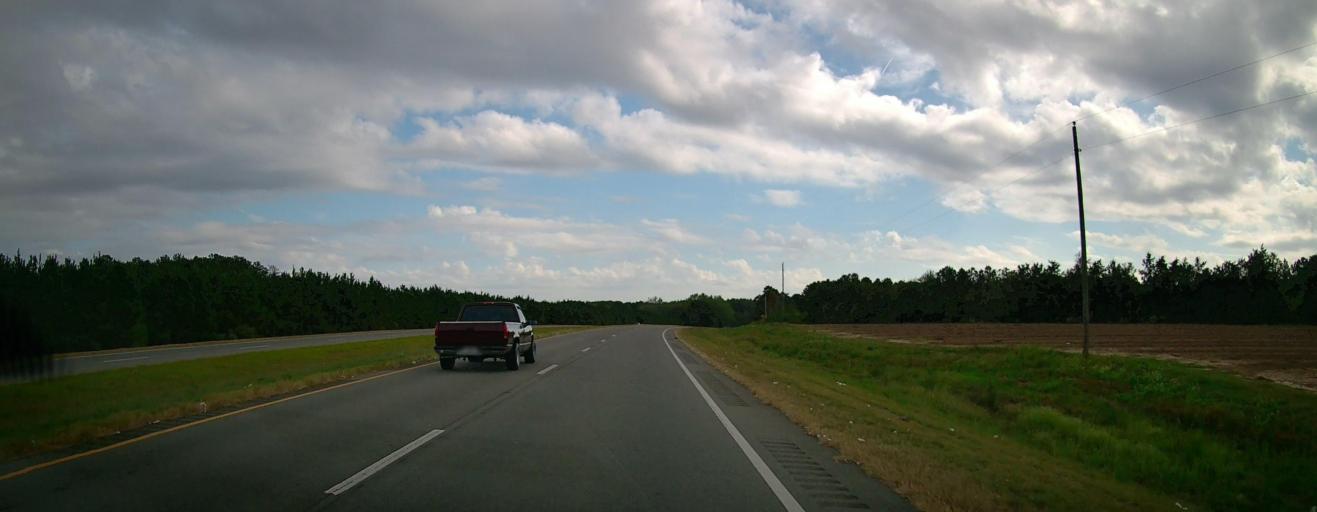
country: US
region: Georgia
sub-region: Thomas County
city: Meigs
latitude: 31.0625
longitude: -84.0733
